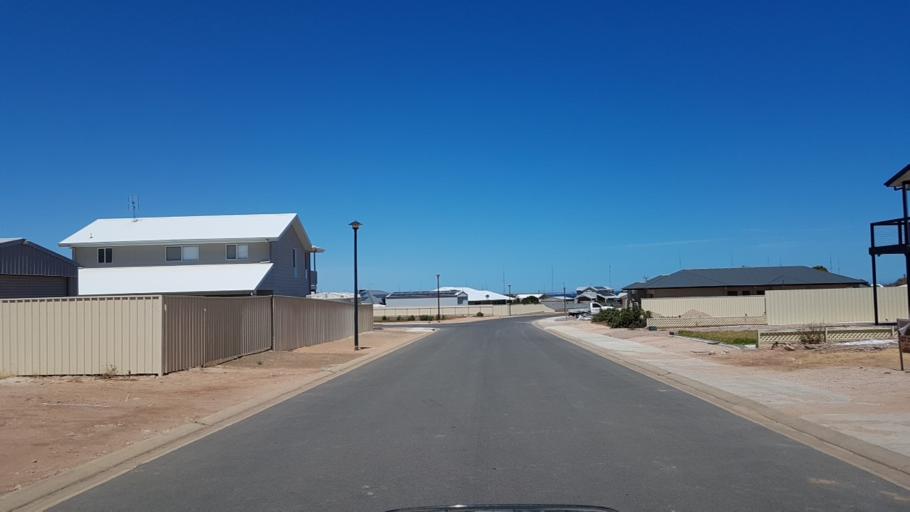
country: AU
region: South Australia
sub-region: Copper Coast
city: Wallaroo
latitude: -33.8925
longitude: 137.6305
